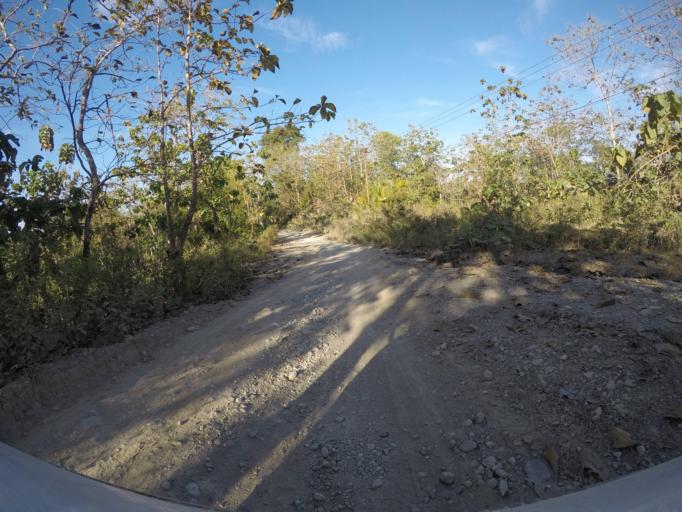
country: TL
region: Viqueque
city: Viqueque
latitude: -8.8729
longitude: 126.3250
